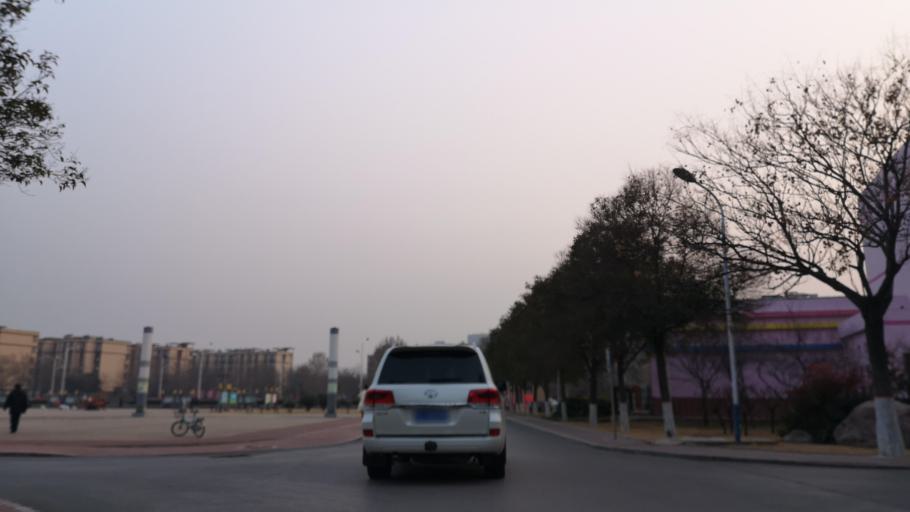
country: CN
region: Henan Sheng
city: Zhongyuanlu
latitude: 35.7850
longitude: 115.0785
